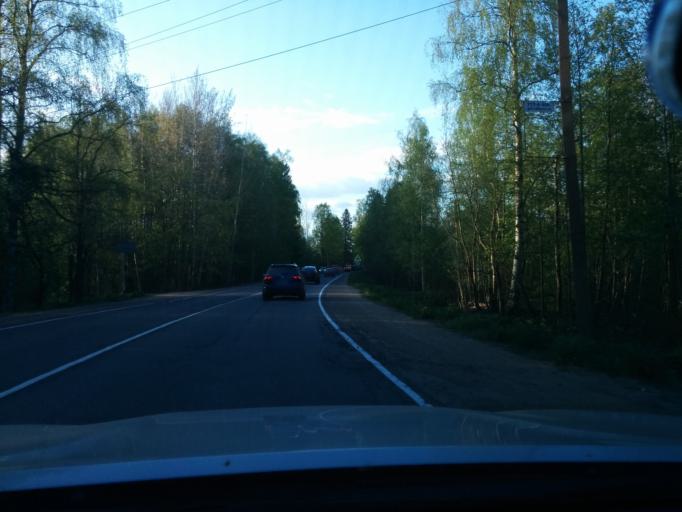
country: RU
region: Leningrad
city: Verkhniye Osel'ki
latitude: 60.2299
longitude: 30.4320
